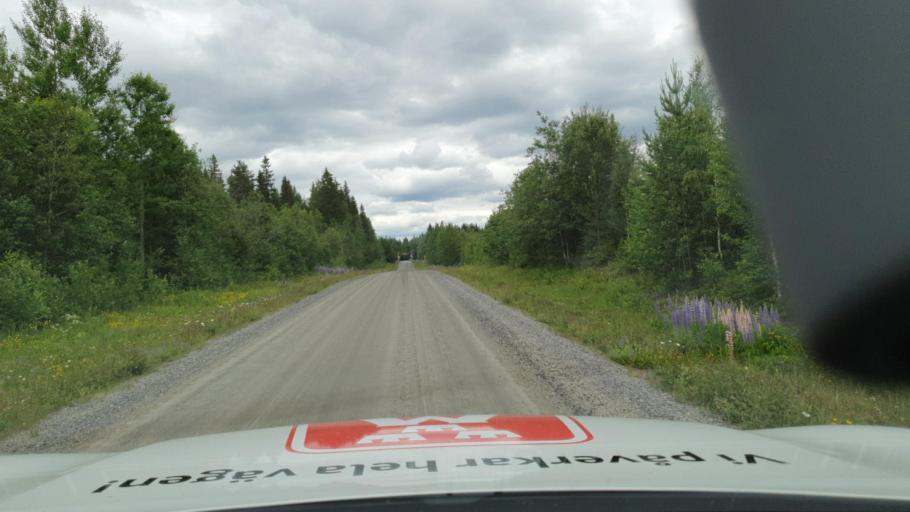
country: SE
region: Vaesterbotten
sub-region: Bjurholms Kommun
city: Bjurholm
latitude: 63.7646
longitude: 19.2623
